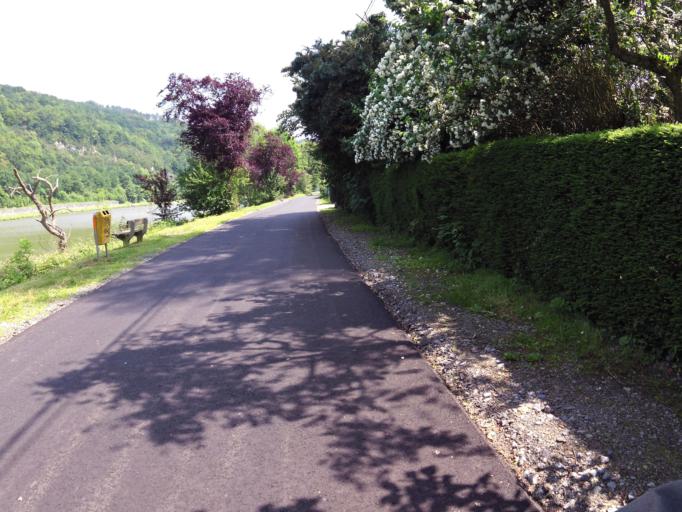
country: BE
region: Wallonia
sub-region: Province de Namur
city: Hastiere-Lavaux
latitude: 50.2152
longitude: 4.8381
